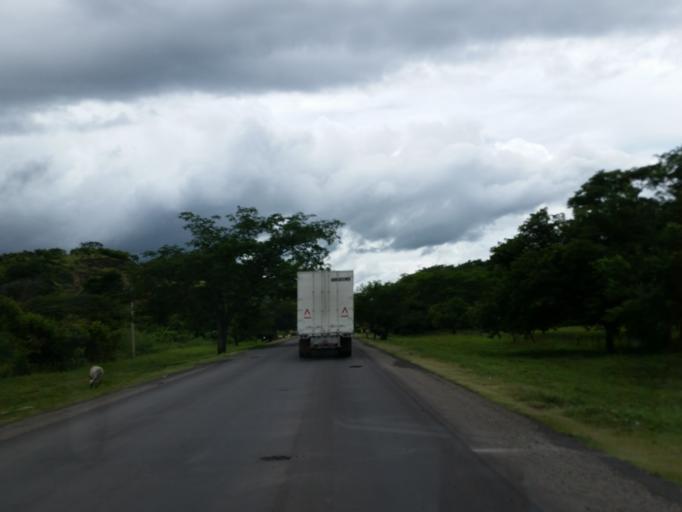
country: NI
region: Chinandega
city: Somotillo
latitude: 12.8701
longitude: -86.8515
